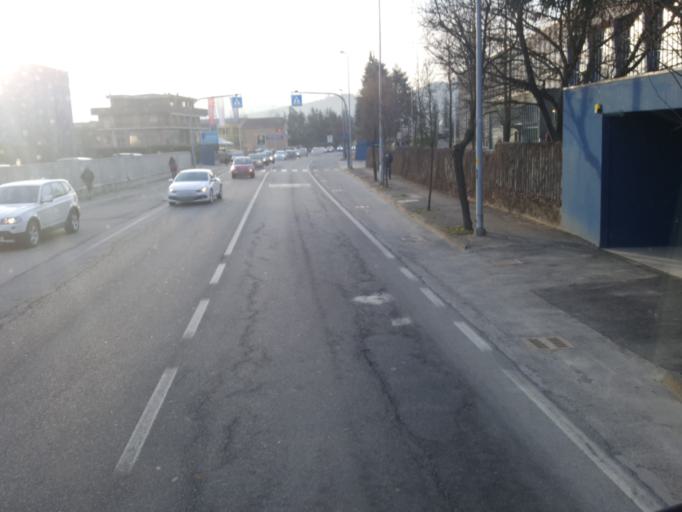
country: IT
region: Piedmont
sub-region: Provincia di Asti
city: Canelli
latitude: 44.7316
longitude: 8.2965
